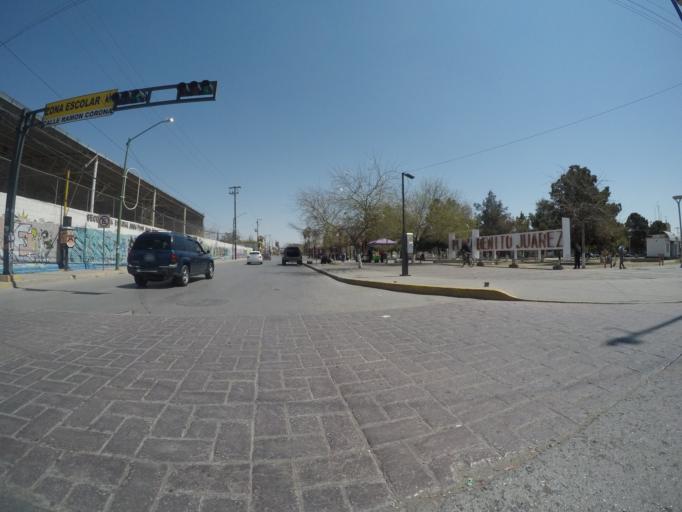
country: MX
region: Chihuahua
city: Ciudad Juarez
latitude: 31.7361
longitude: -106.4805
